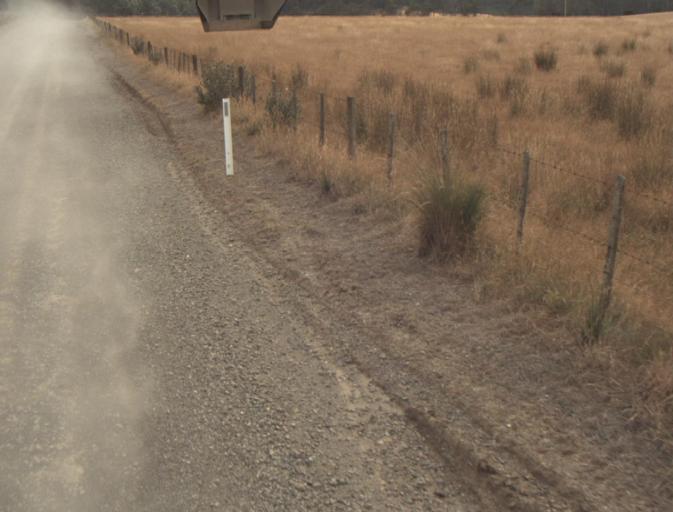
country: AU
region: Tasmania
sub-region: Northern Midlands
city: Evandale
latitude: -41.4708
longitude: 147.4467
